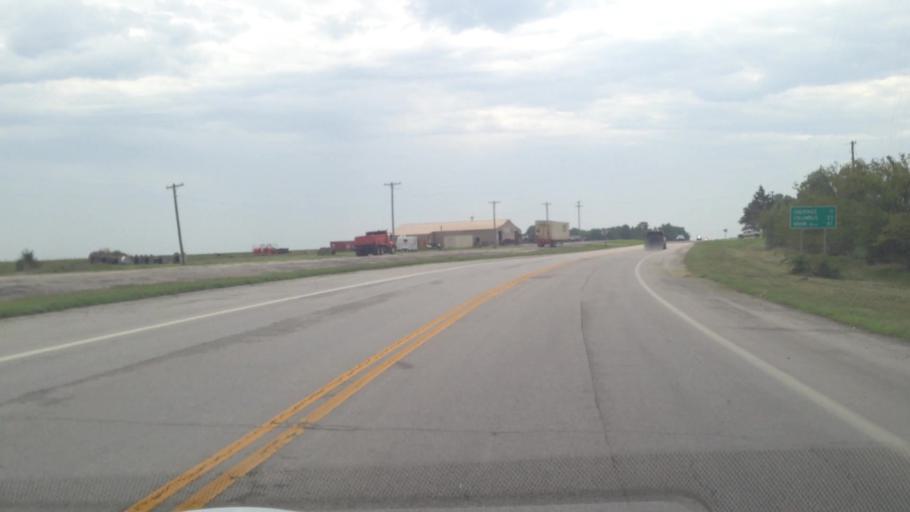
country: US
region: Kansas
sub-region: Crawford County
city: Girard
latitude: 37.4985
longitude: -94.8428
